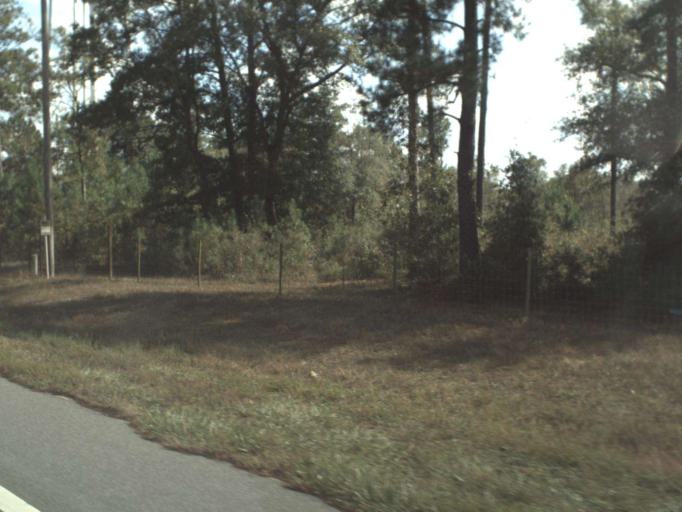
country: US
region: Florida
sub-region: Gadsden County
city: Gretna
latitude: 30.6909
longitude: -84.7298
